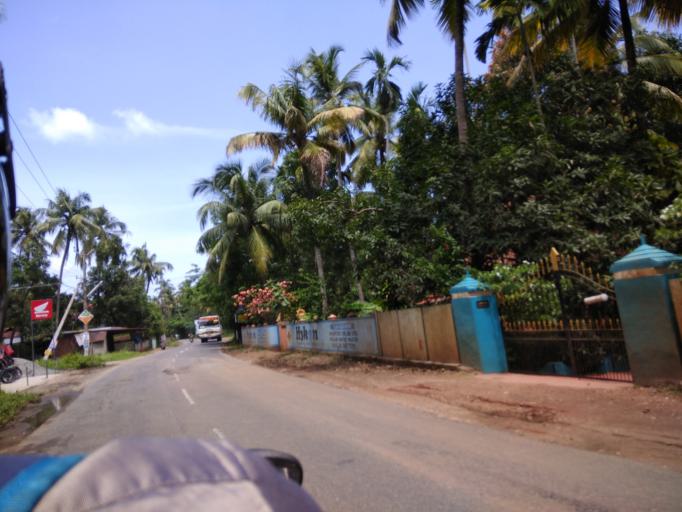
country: IN
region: Kerala
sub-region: Thrissur District
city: Thanniyam
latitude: 10.4895
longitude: 76.1365
